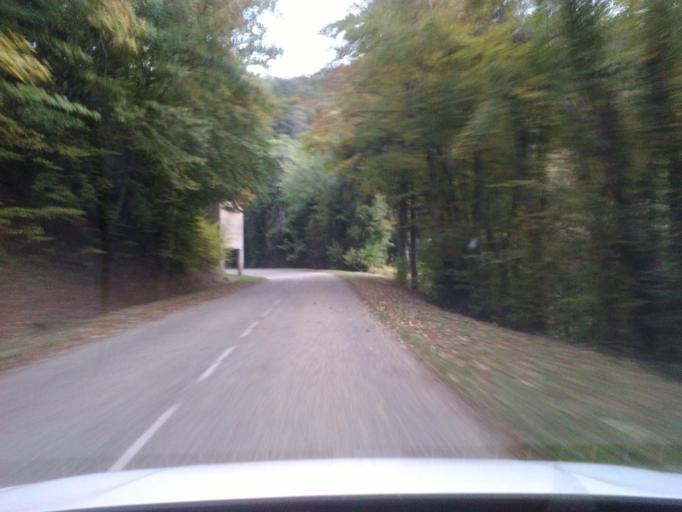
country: FR
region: Lorraine
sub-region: Departement des Vosges
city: Ban-de-Laveline
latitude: 48.3641
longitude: 7.1051
